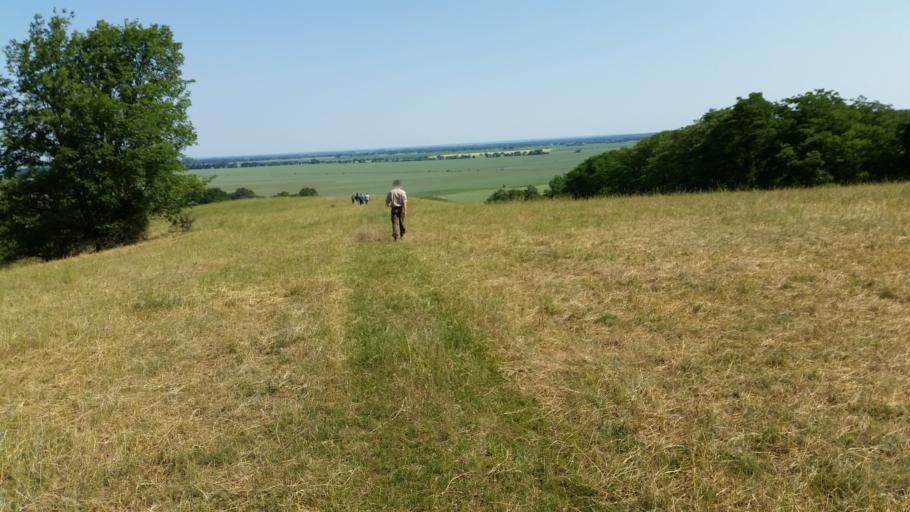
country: DE
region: Brandenburg
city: Podelzig
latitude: 52.4629
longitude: 14.4928
